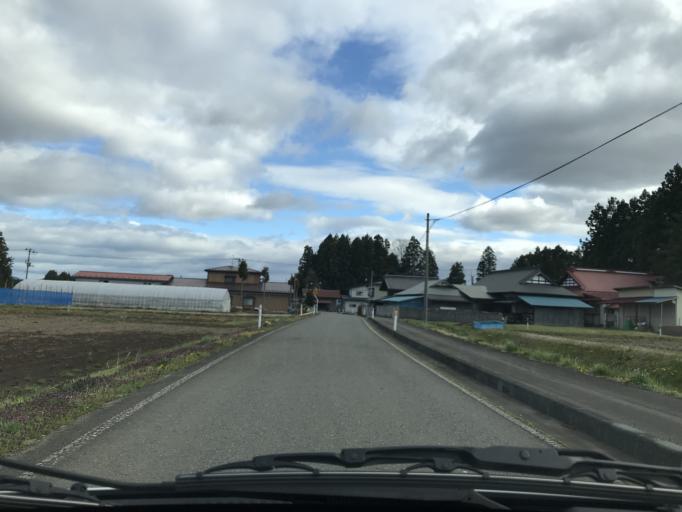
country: JP
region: Iwate
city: Mizusawa
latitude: 39.1280
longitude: 141.0878
